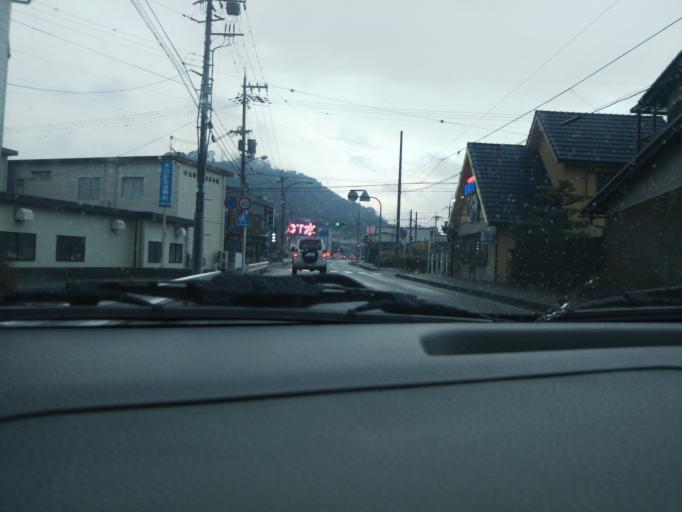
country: JP
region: Shiga Prefecture
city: Minakuchicho-matoba
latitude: 34.9737
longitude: 136.1738
